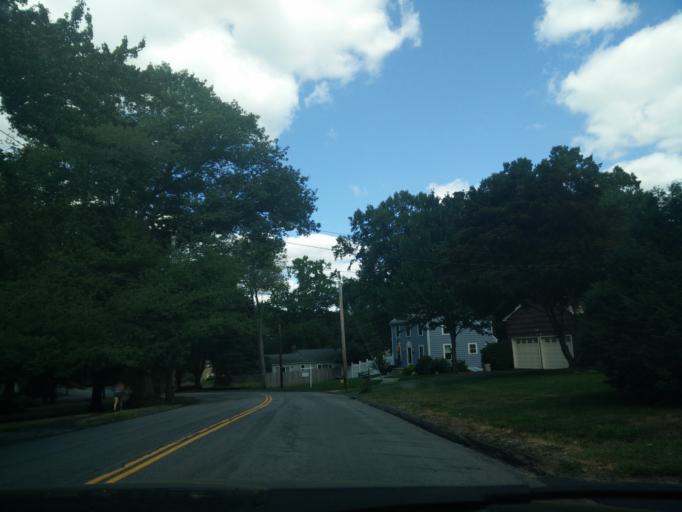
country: US
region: Connecticut
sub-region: Fairfield County
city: Bridgeport
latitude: 41.1929
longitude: -73.2347
